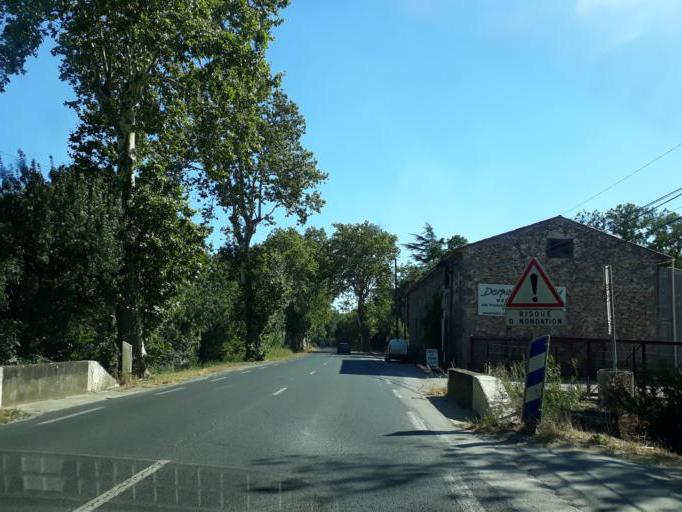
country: FR
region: Languedoc-Roussillon
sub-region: Departement de l'Herault
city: Agde
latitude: 43.3232
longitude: 3.4777
